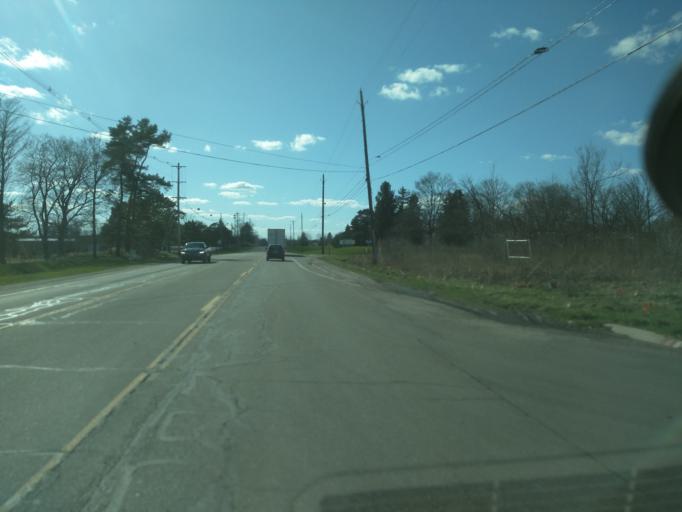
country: US
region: Michigan
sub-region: Eaton County
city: Waverly
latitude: 42.7784
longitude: -84.6362
